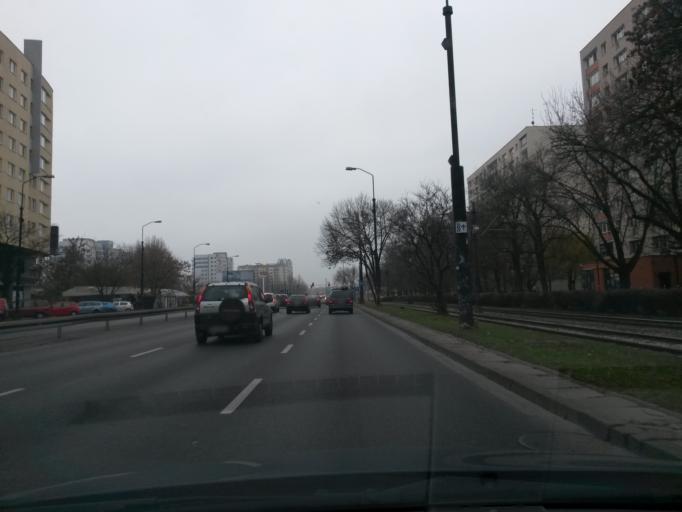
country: PL
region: Masovian Voivodeship
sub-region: Warszawa
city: Mokotow
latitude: 52.1753
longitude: 21.0206
